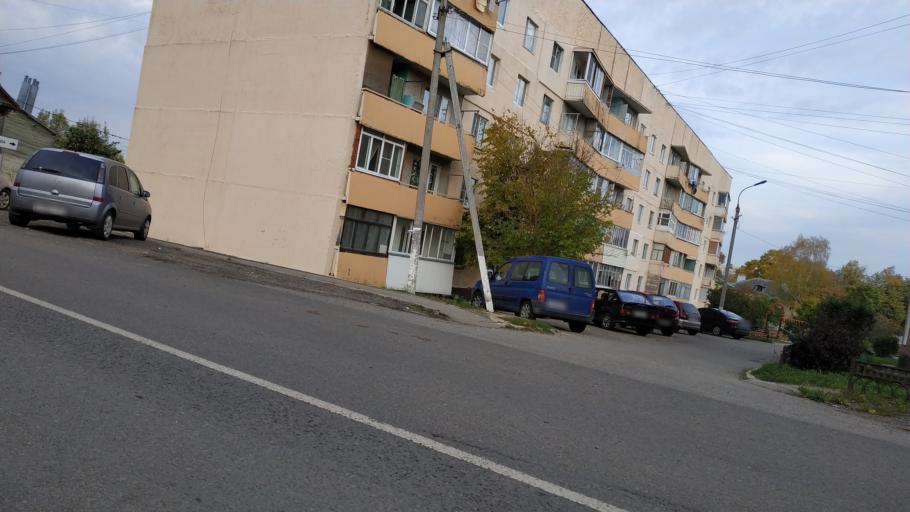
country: RU
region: Moskovskaya
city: Mozhaysk
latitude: 55.5084
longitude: 36.0209
